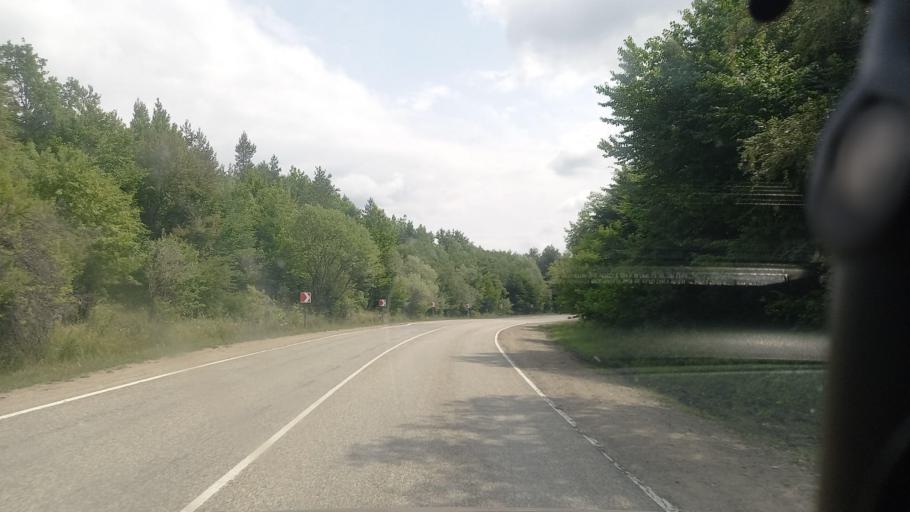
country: RU
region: Karachayevo-Cherkesiya
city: Kurdzhinovo
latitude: 44.0389
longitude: 40.9118
